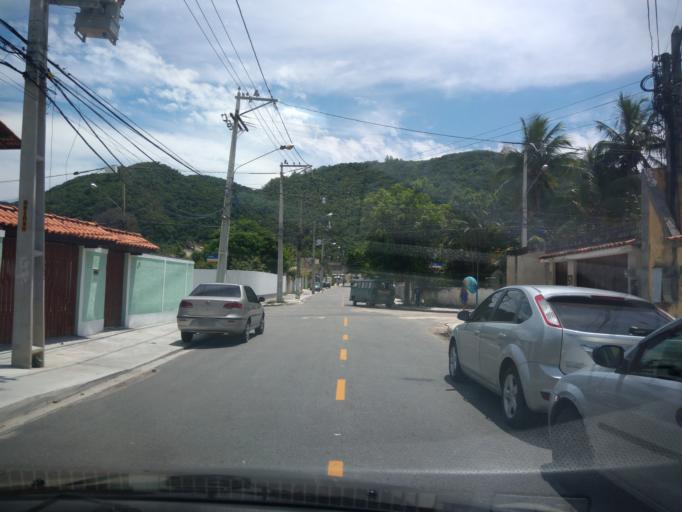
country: BR
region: Rio de Janeiro
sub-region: Niteroi
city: Niteroi
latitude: -22.9320
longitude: -43.0679
